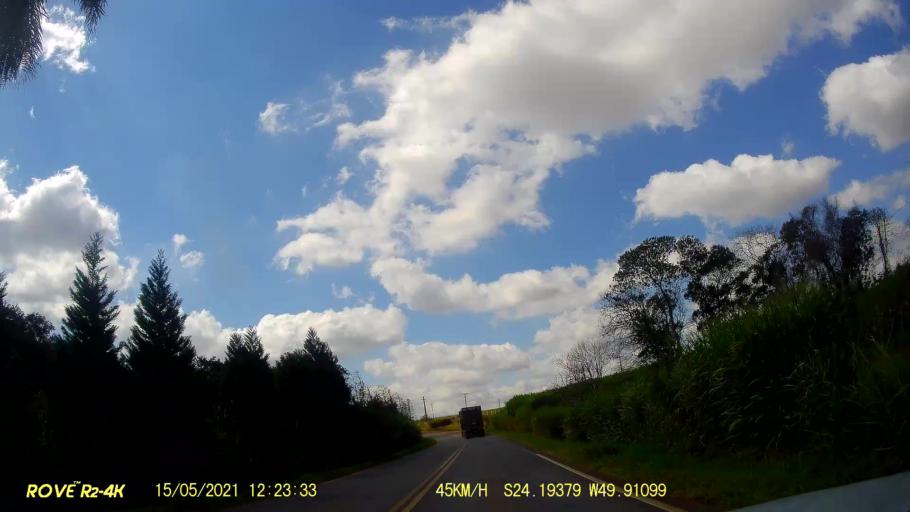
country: BR
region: Parana
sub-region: Jaguariaiva
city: Jaguariaiva
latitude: -24.1938
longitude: -49.9110
